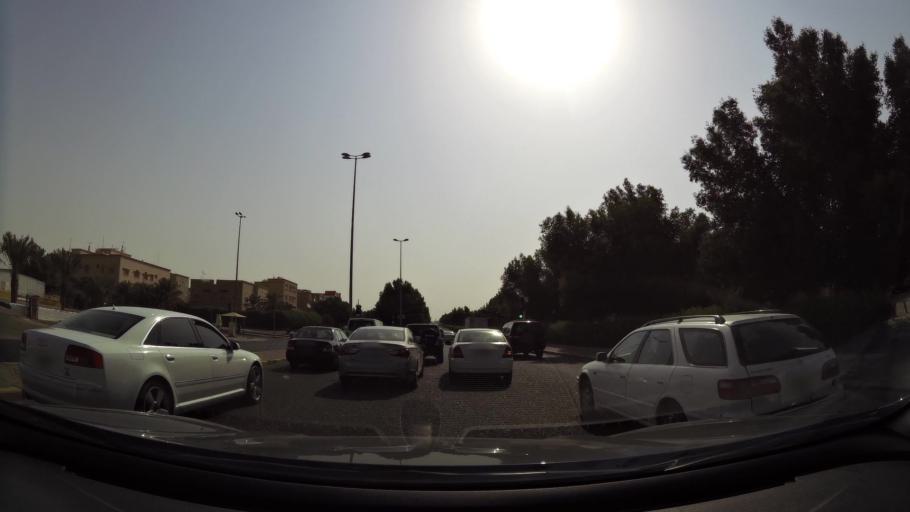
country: KW
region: Muhafazat al Jahra'
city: Al Jahra'
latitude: 29.3250
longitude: 47.6613
